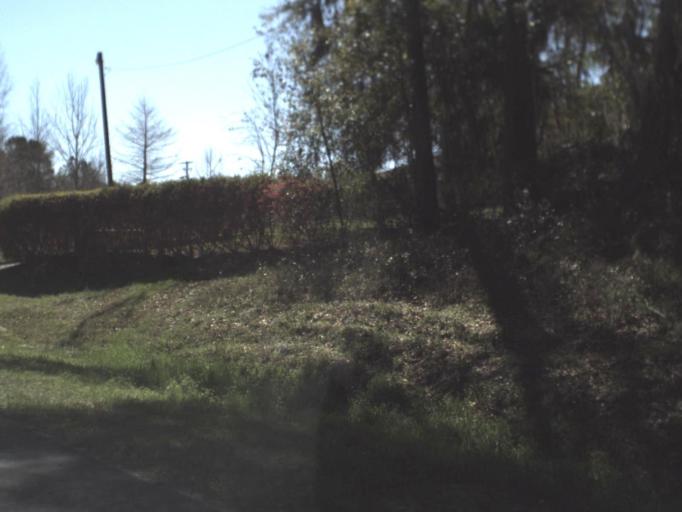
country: US
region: Florida
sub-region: Gadsden County
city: Midway
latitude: 30.5060
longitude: -84.3619
